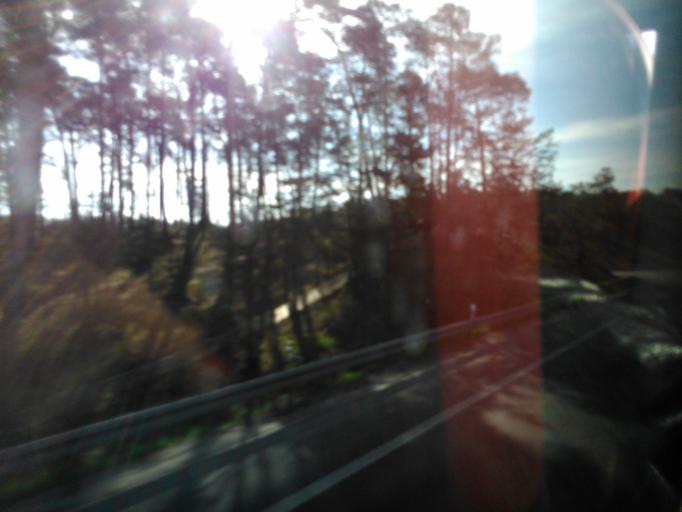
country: PL
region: Kujawsko-Pomorskie
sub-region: Powiat aleksandrowski
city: Aleksandrow Kujawski
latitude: 52.9278
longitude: 18.7080
